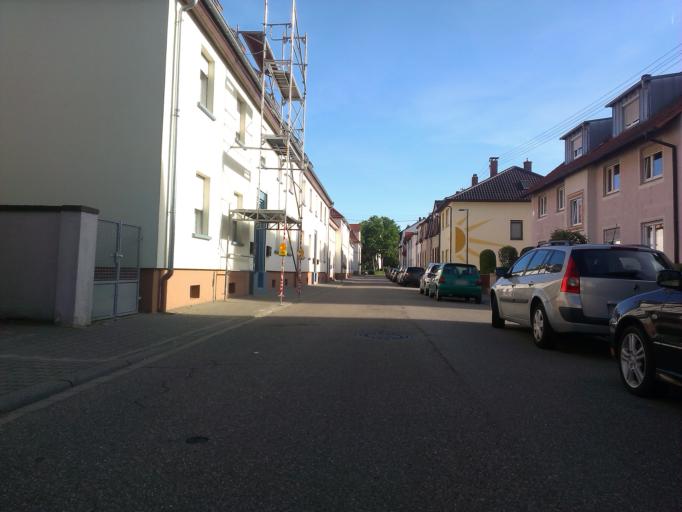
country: DE
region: Baden-Wuerttemberg
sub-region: Karlsruhe Region
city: Edingen-Neckarhausen
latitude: 49.4394
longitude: 8.5793
